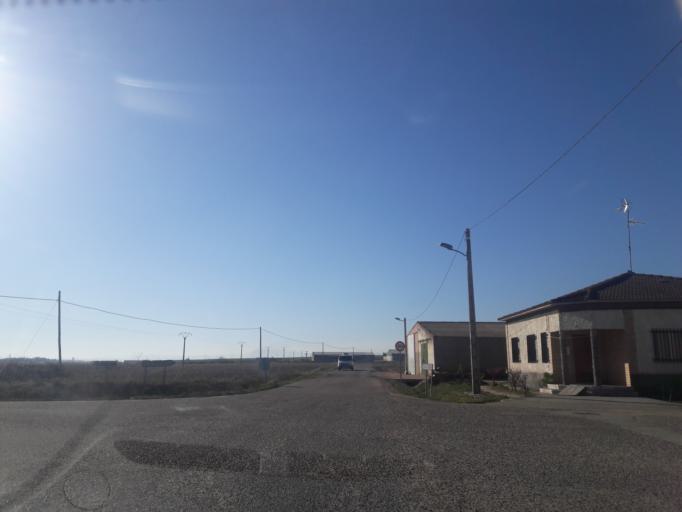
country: ES
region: Castille and Leon
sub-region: Provincia de Salamanca
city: Penarandilla
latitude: 40.8801
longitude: -5.3915
